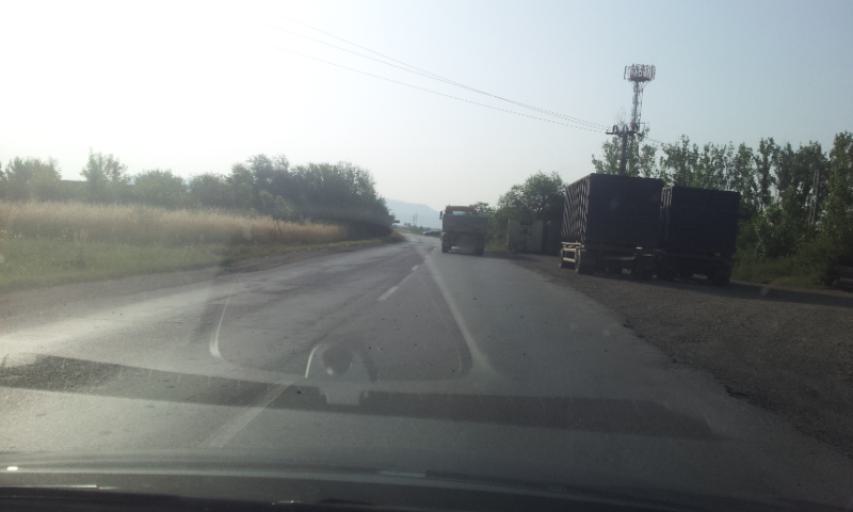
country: SK
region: Kosicky
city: Kosice
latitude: 48.6178
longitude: 21.2345
